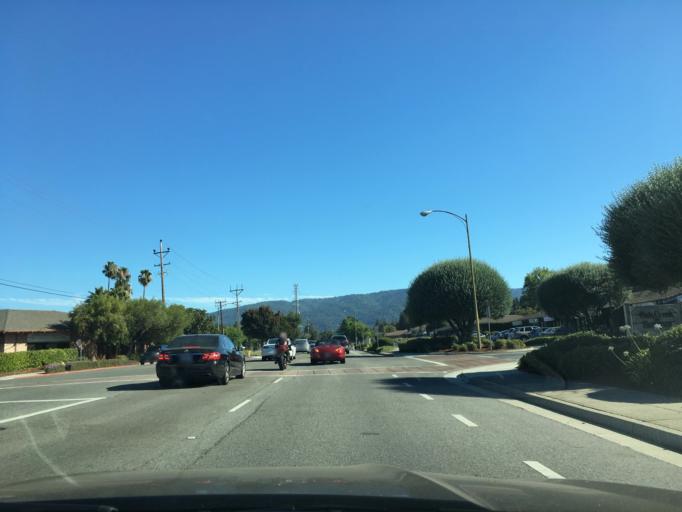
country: US
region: California
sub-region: Santa Clara County
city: Saratoga
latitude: 37.2918
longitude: -122.0324
